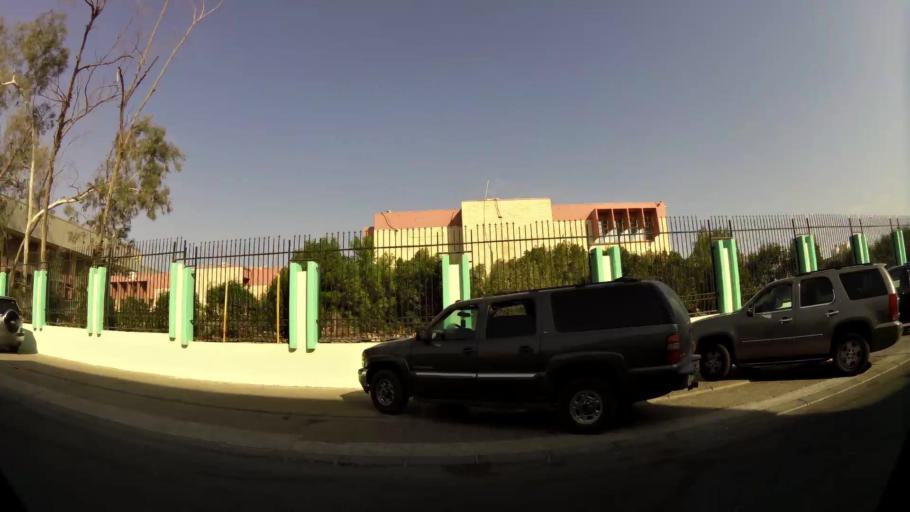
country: KW
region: Al Ahmadi
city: Ar Riqqah
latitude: 29.1582
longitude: 48.0685
